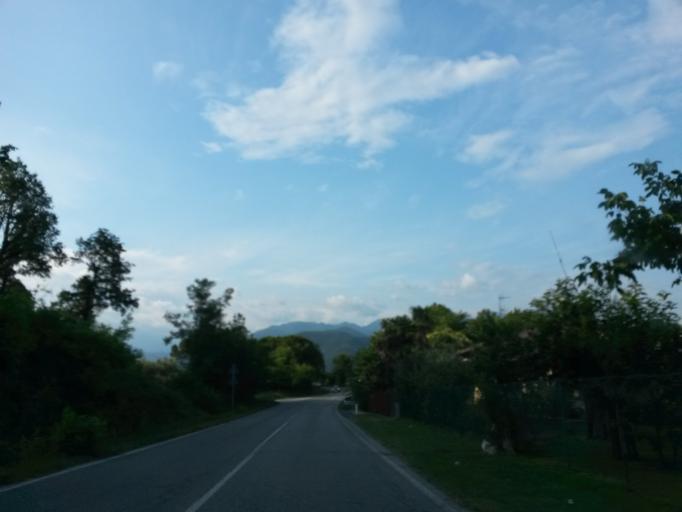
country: IT
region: Lombardy
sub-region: Provincia di Brescia
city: Cunettone-Villa
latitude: 45.5797
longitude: 10.5154
